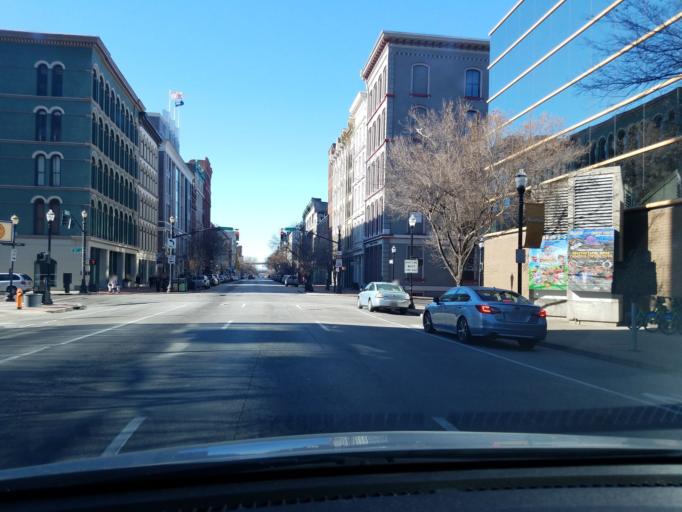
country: US
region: Kentucky
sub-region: Jefferson County
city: Louisville
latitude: 38.2570
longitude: -85.7593
